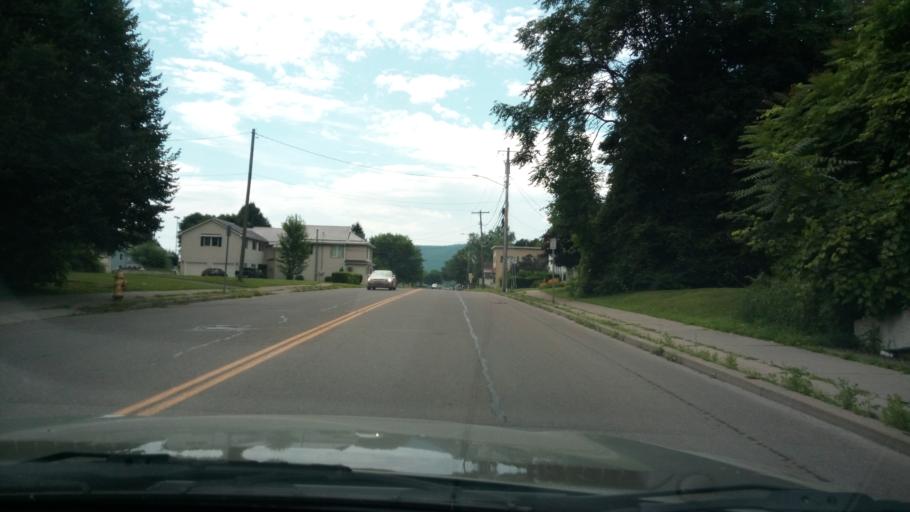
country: US
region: New York
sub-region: Chemung County
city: Elmira
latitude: 42.0734
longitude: -76.8005
